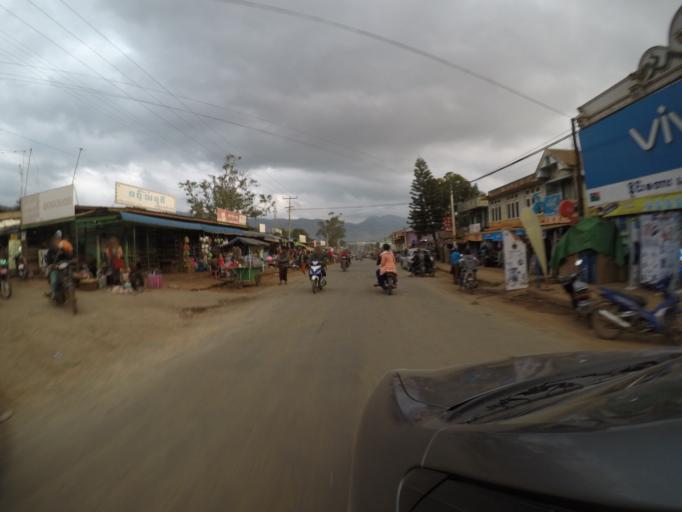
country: MM
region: Shan
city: Taunggyi
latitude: 20.7775
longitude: 96.9984
